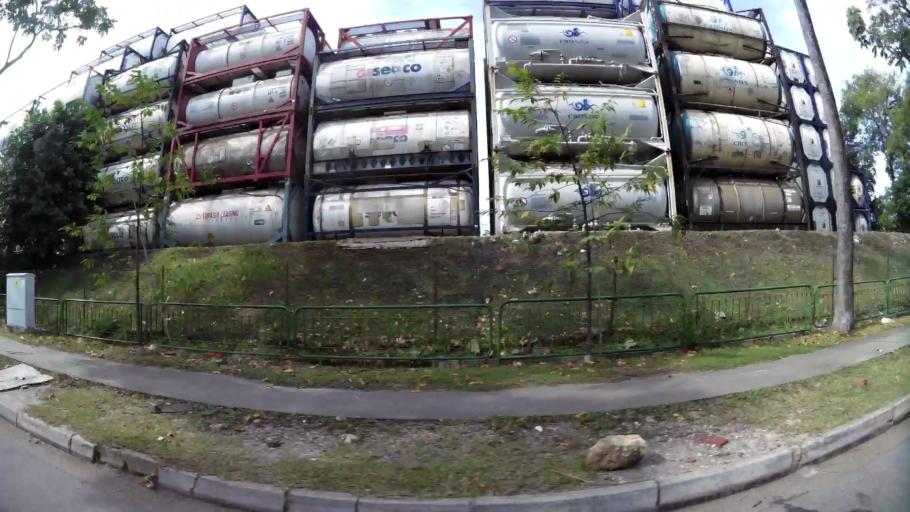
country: MY
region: Johor
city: Johor Bahru
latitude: 1.3224
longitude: 103.6445
